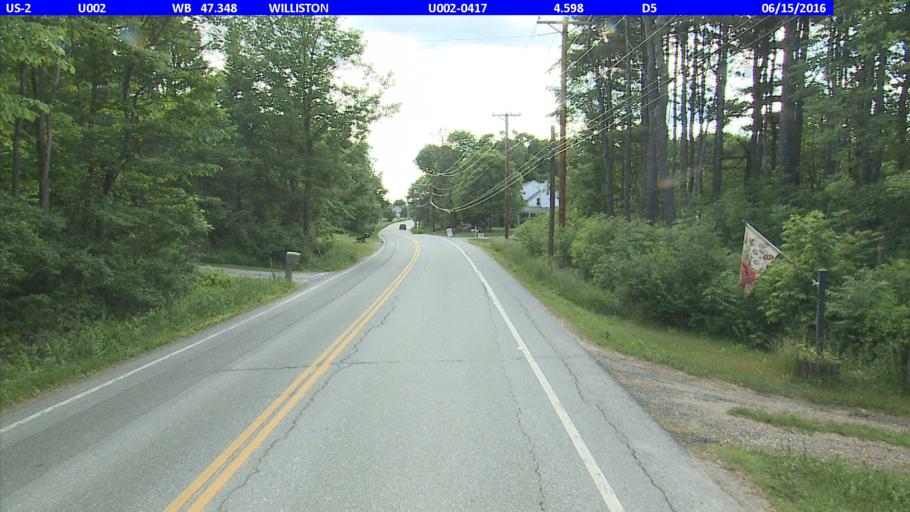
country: US
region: Vermont
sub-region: Chittenden County
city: Williston
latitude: 44.4347
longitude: -73.0513
